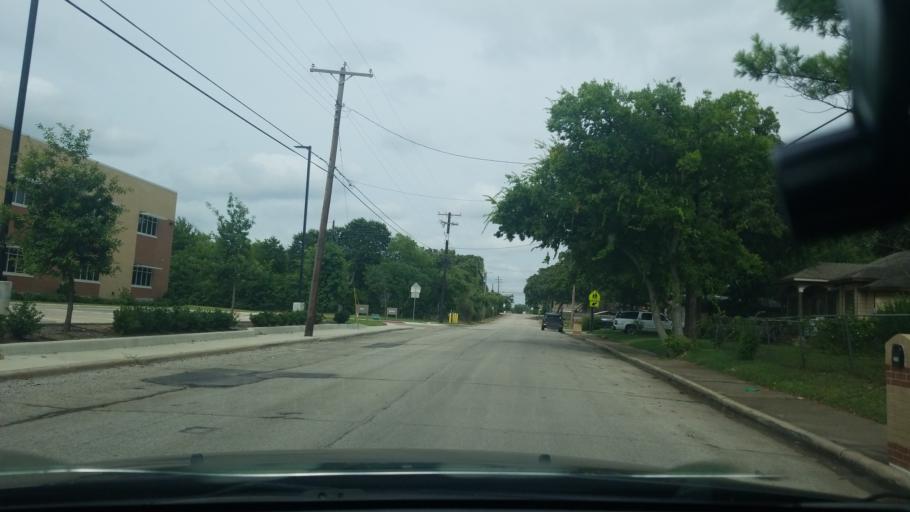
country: US
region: Texas
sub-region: Dallas County
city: Balch Springs
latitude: 32.7574
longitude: -96.6337
